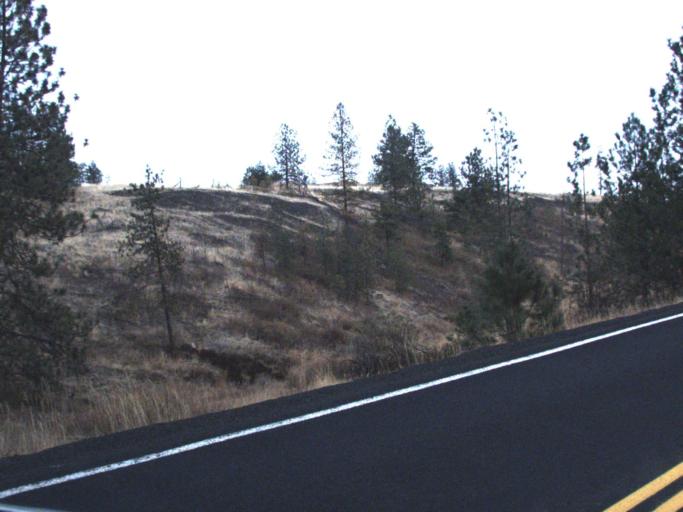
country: US
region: Washington
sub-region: Lincoln County
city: Davenport
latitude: 47.8639
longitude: -118.2484
